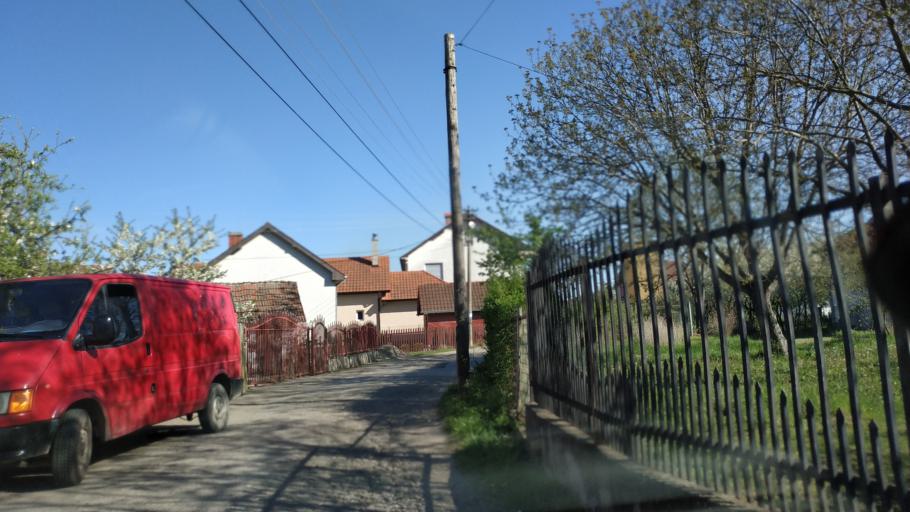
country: RS
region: Central Serbia
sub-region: Nisavski Okrug
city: Aleksinac
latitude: 43.5115
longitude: 21.6943
